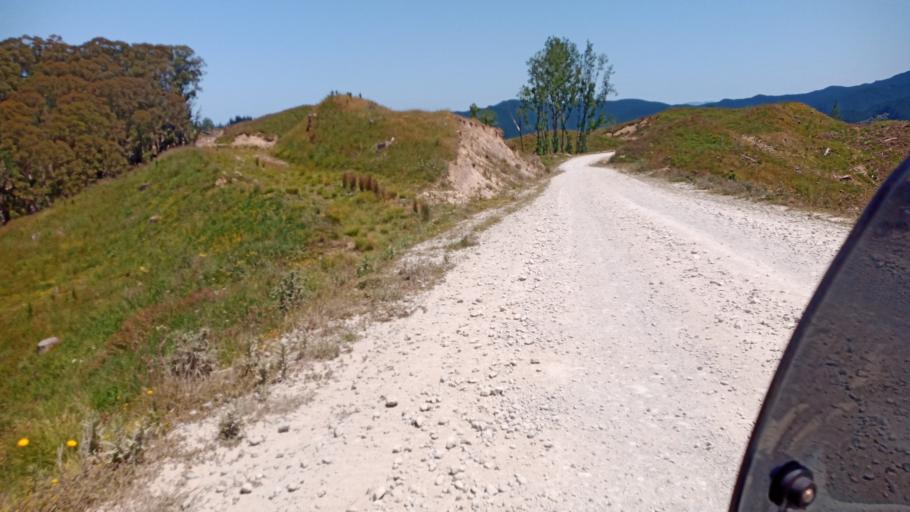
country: NZ
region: Gisborne
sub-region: Gisborne District
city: Gisborne
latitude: -38.2899
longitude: 178.0155
